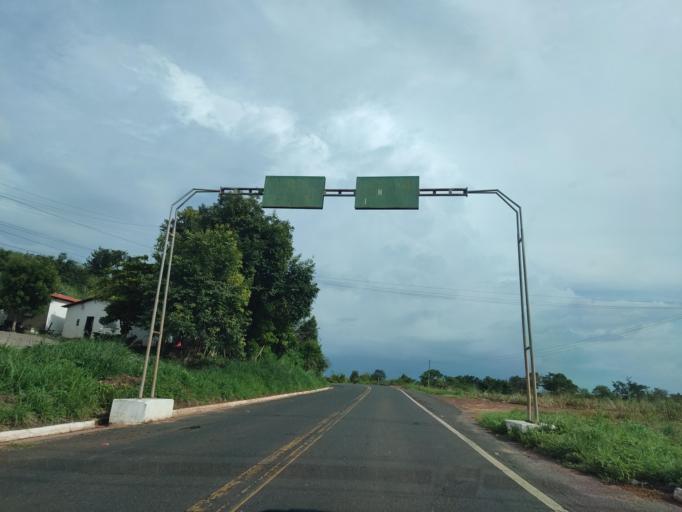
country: BR
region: Piaui
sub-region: Agua Branca
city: Agua Branca
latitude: -5.8240
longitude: -42.5058
